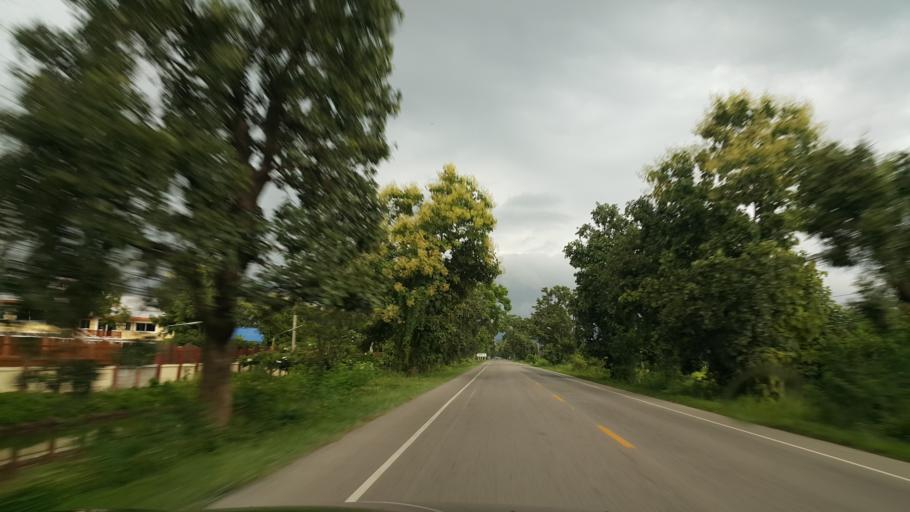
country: TH
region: Phayao
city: Dok Kham Tai
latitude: 19.2173
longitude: 100.0411
